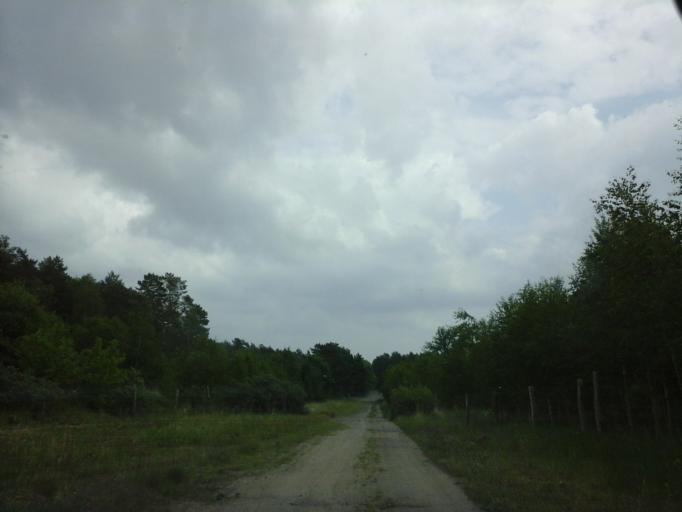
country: PL
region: West Pomeranian Voivodeship
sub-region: Powiat walecki
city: Tuczno
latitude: 53.2291
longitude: 16.0565
